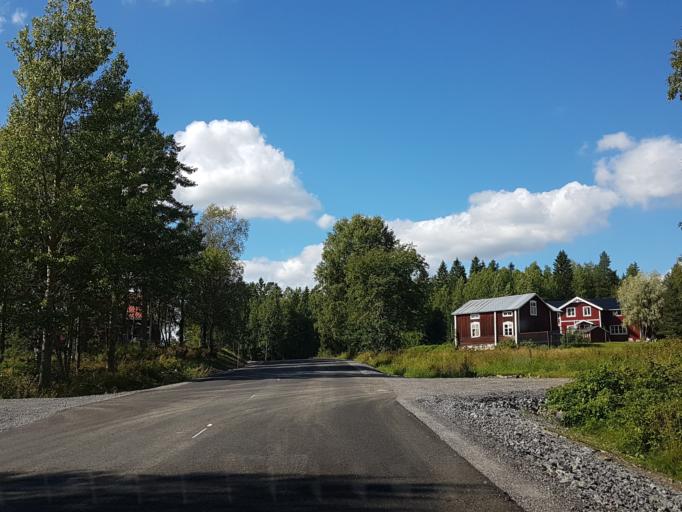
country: SE
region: Vaesterbotten
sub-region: Robertsfors Kommun
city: Robertsfors
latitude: 64.1376
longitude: 20.6254
